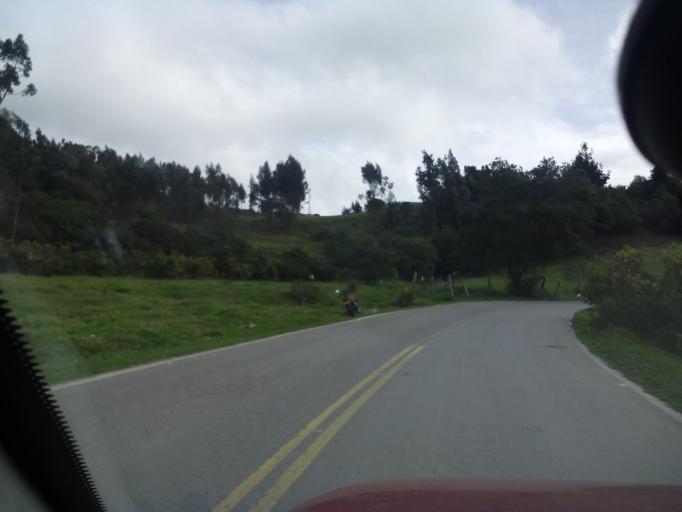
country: CO
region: Boyaca
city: Combita
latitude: 5.6330
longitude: -73.3414
